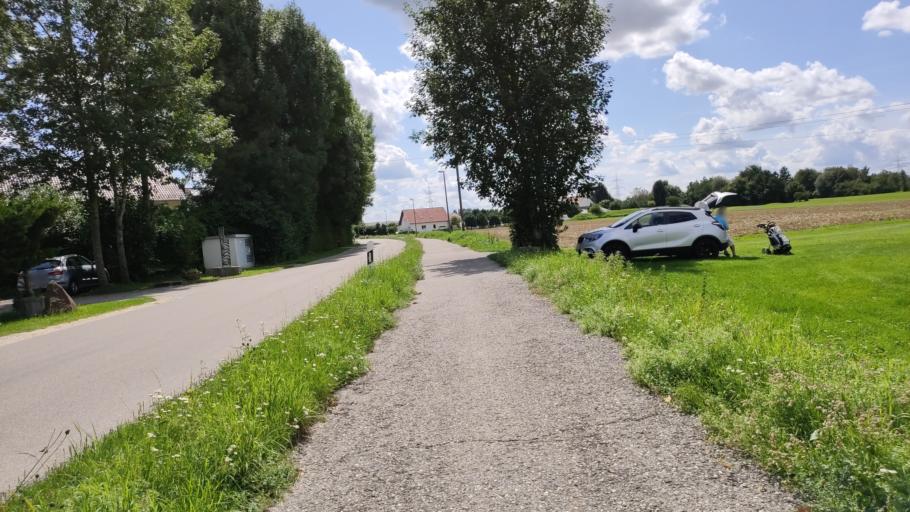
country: DE
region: Bavaria
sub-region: Swabia
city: Konigsbrunn
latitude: 48.2429
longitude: 10.8933
